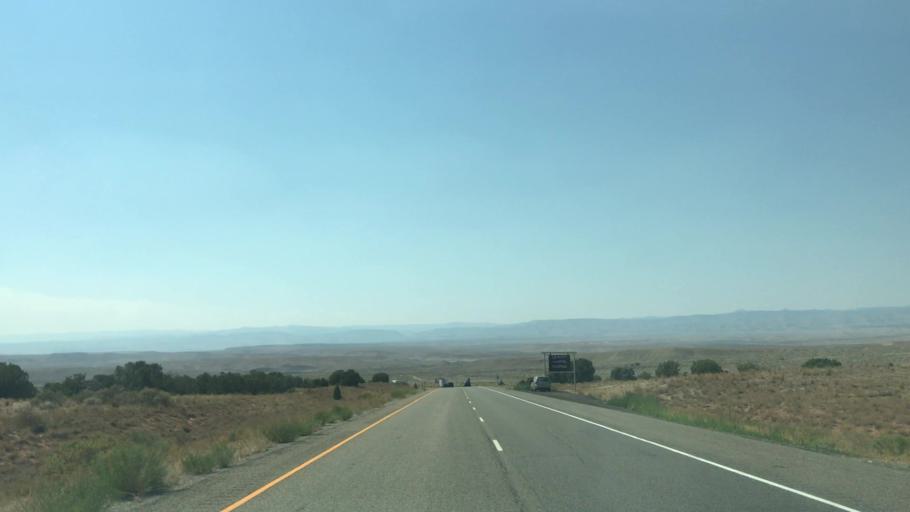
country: US
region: Colorado
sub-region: Mesa County
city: Loma
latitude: 39.1925
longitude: -109.0467
